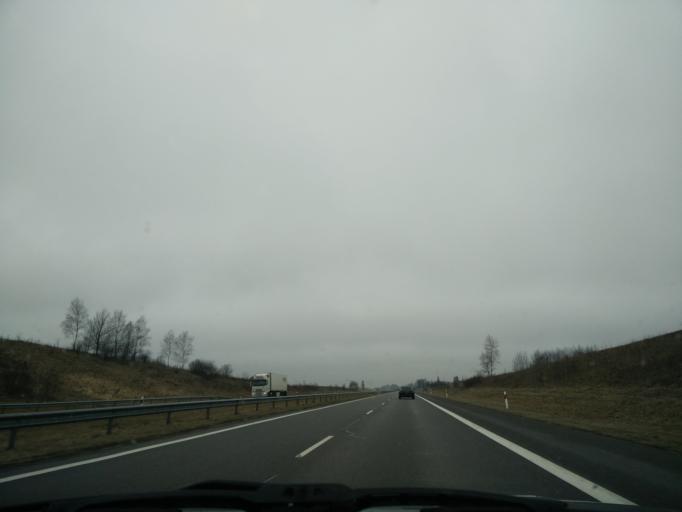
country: LT
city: Skaudvile
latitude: 55.4503
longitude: 22.7140
